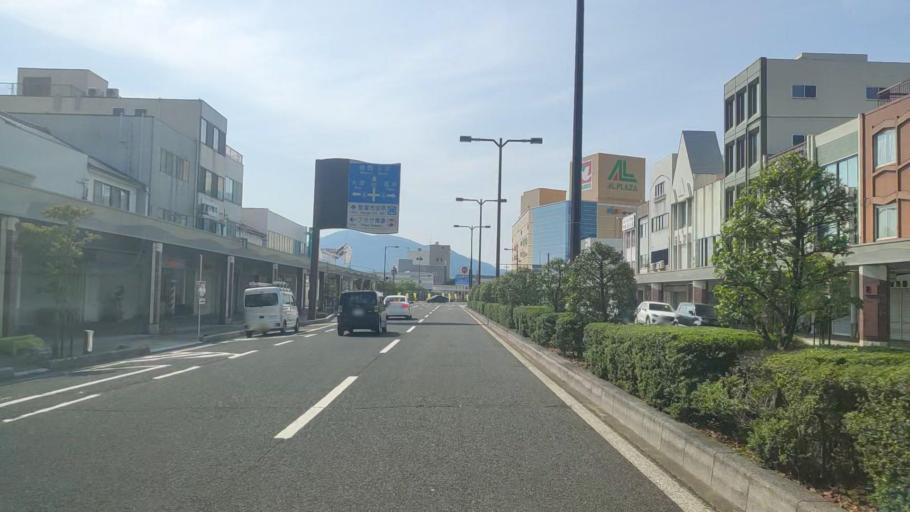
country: JP
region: Fukui
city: Tsuruga
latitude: 35.6467
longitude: 136.0735
